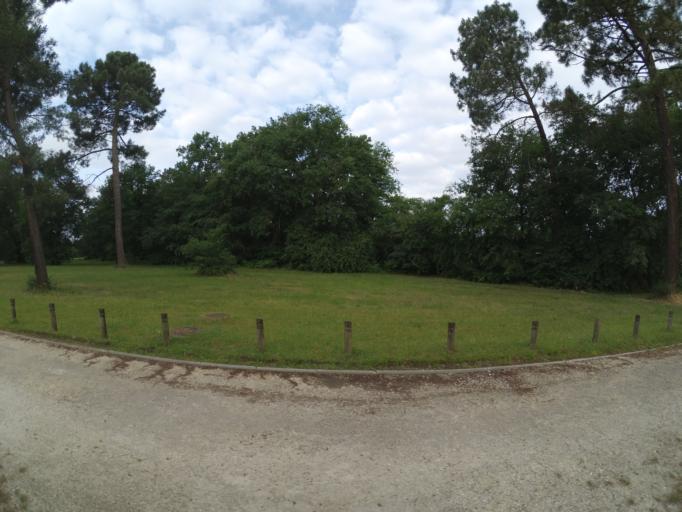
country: FR
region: Aquitaine
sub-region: Departement de la Gironde
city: Pessac
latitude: 44.7984
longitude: -0.6843
